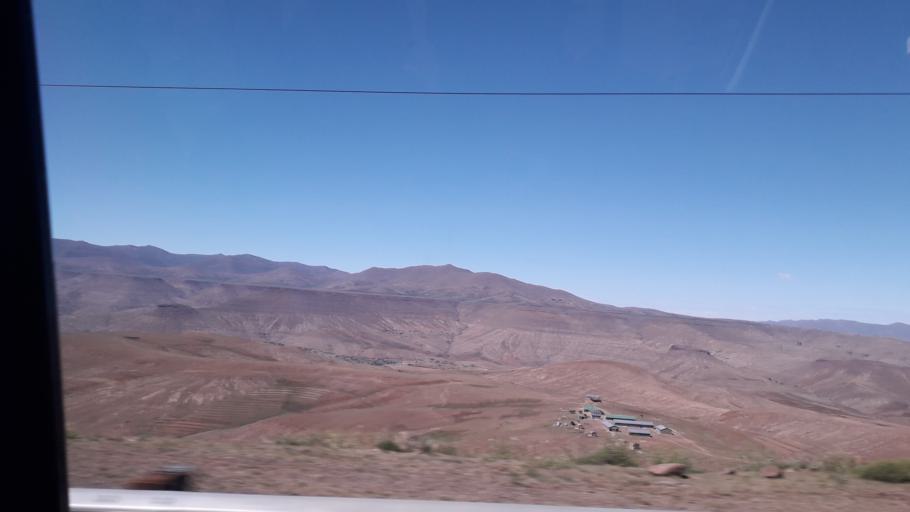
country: LS
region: Mokhotlong
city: Mokhotlong
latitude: -29.2843
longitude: 28.9463
